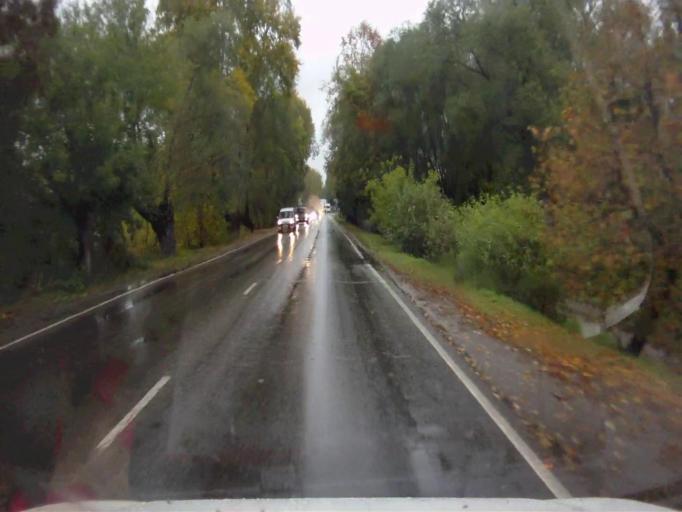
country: RU
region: Chelyabinsk
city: Kyshtym
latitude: 55.7180
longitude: 60.5422
